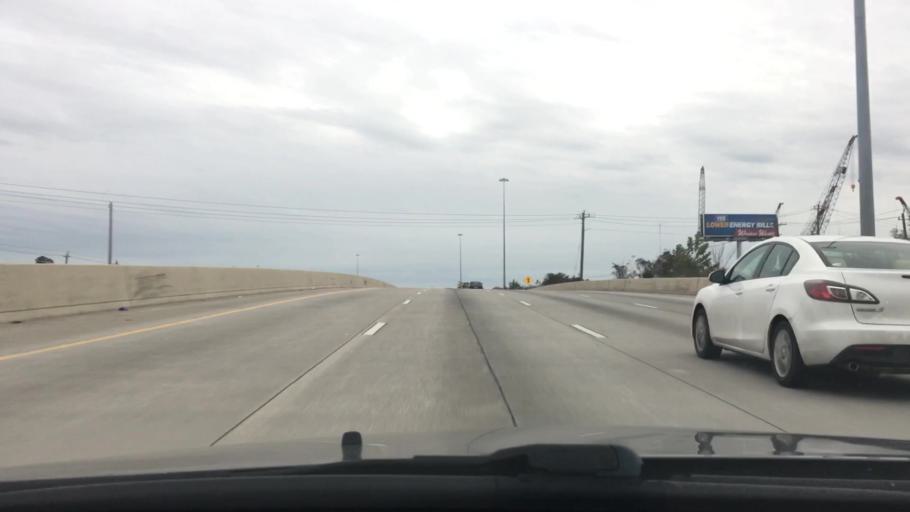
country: US
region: Texas
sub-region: Harris County
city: Houston
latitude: 29.8080
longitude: -95.3027
